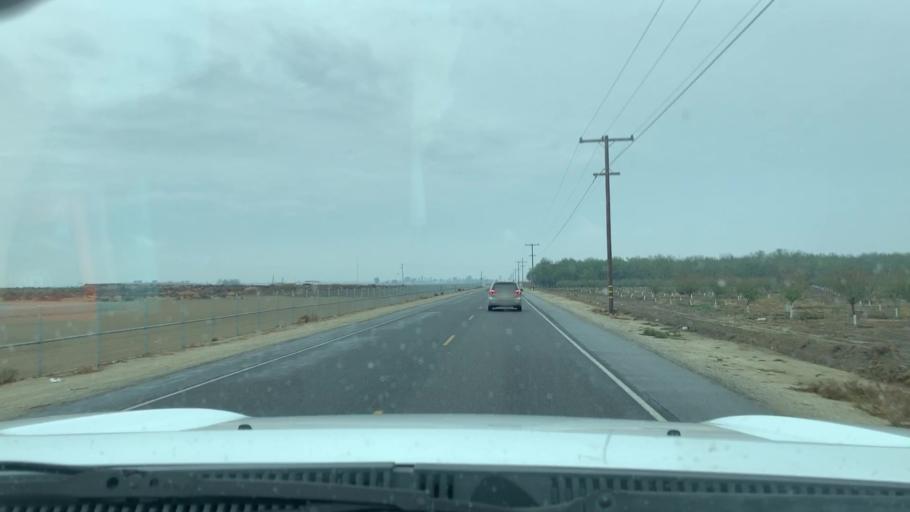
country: US
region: California
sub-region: Kern County
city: Delano
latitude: 35.7613
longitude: -119.3162
